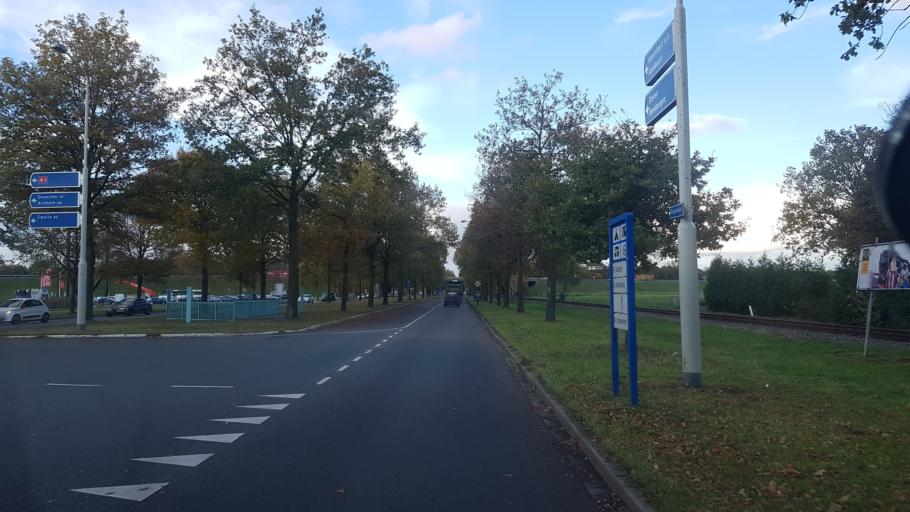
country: NL
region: Gelderland
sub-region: Gemeente Apeldoorn
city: Beekbergen
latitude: 52.1734
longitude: 5.9824
